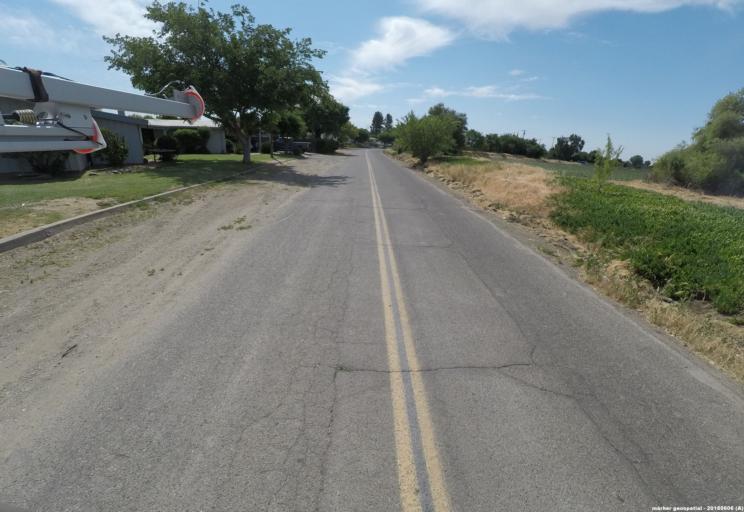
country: US
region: California
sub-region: Fresno County
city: Firebaugh
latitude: 36.8549
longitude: -120.4373
